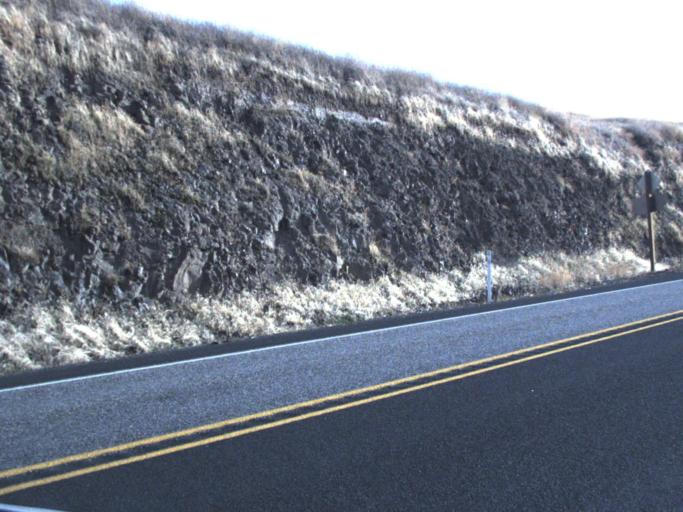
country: US
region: Washington
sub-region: Columbia County
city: Dayton
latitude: 46.4263
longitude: -117.9471
